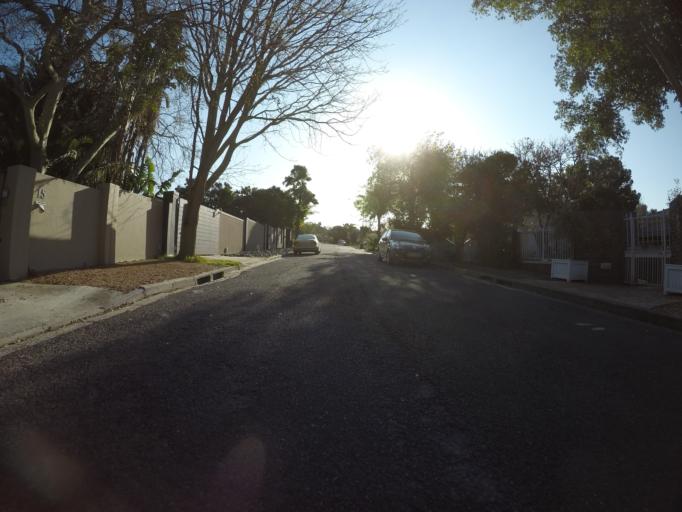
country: ZA
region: Western Cape
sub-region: City of Cape Town
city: Kraaifontein
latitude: -33.8595
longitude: 18.6511
